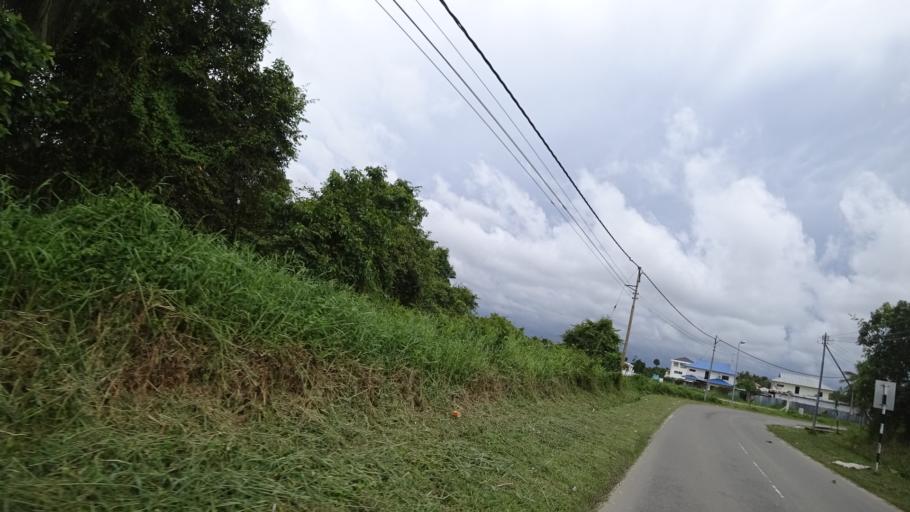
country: BN
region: Brunei and Muara
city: Bandar Seri Begawan
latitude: 4.8556
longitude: 114.8542
